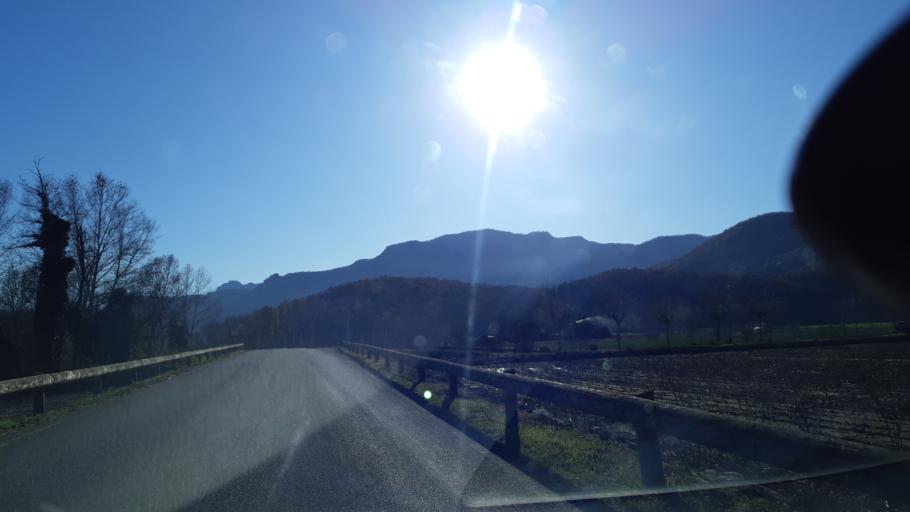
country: ES
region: Catalonia
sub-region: Provincia de Girona
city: Bas
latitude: 42.1442
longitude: 2.4407
